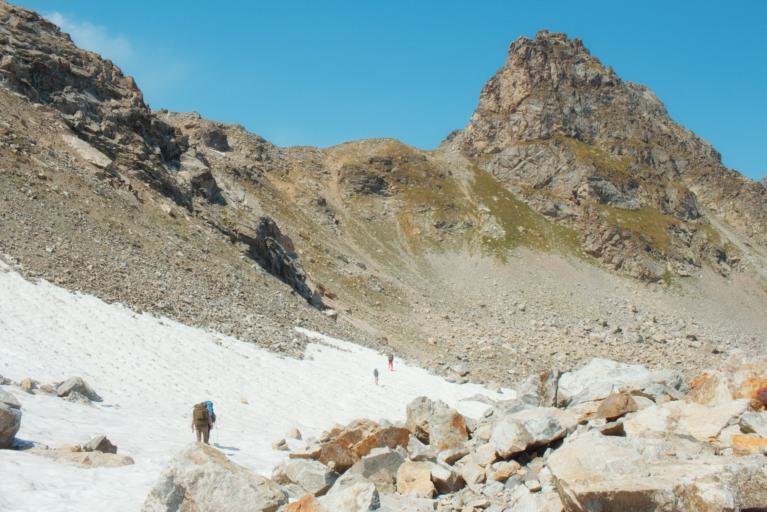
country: RU
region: Karachayevo-Cherkesiya
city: Nizhniy Arkhyz
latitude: 43.4568
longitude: 41.2235
